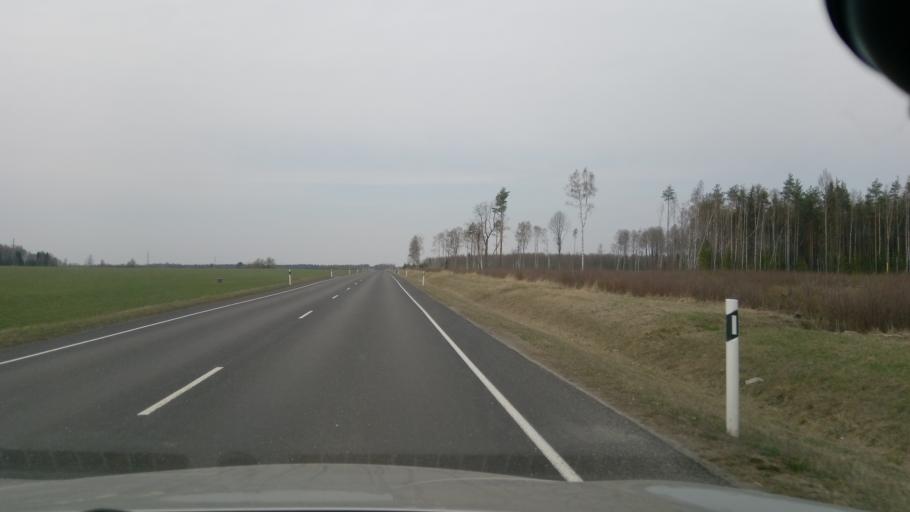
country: EE
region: Viljandimaa
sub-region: Vohma linn
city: Vohma
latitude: 58.7225
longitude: 25.6038
